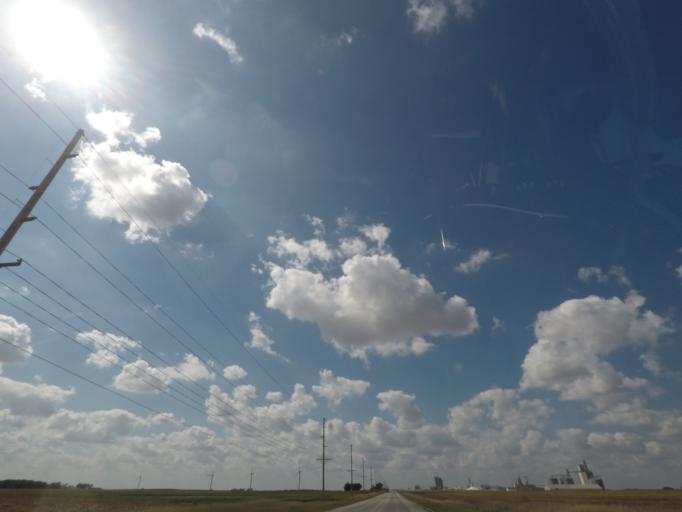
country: US
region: Iowa
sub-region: Story County
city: Nevada
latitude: 42.0230
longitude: -93.4901
